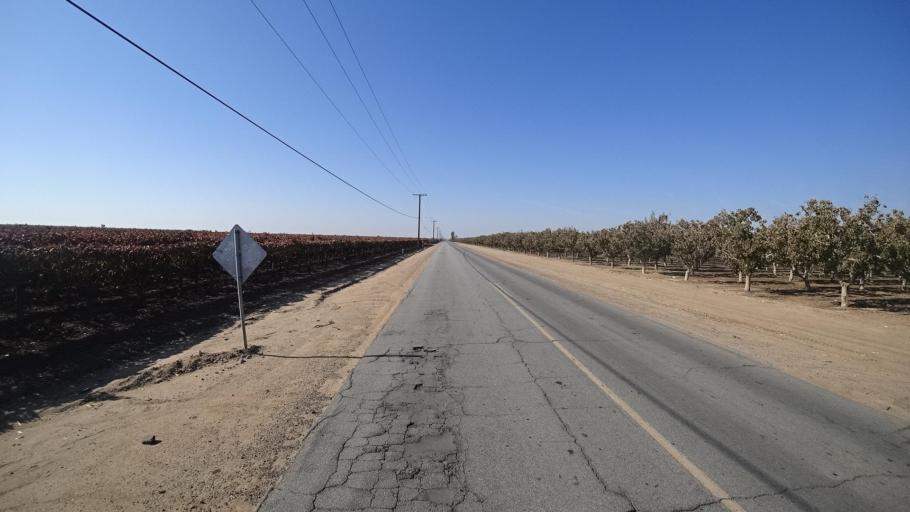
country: US
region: California
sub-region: Kern County
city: McFarland
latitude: 35.7179
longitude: -119.1898
